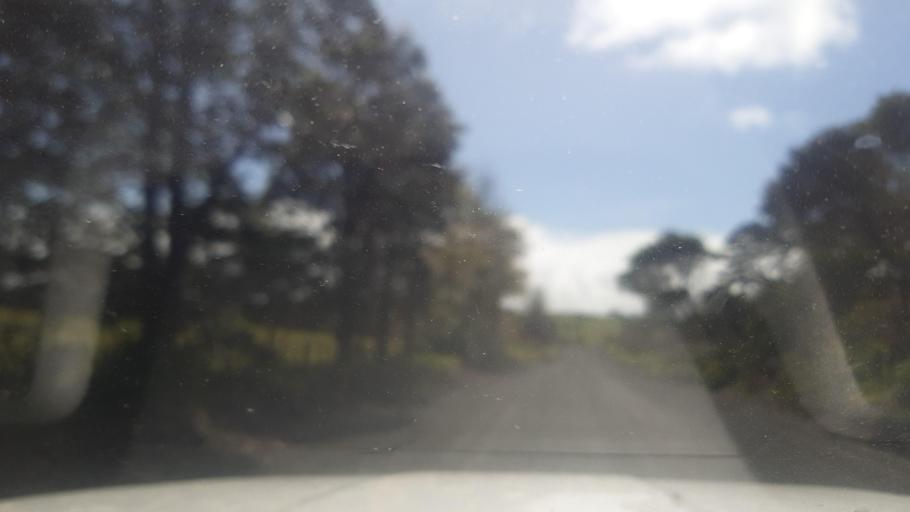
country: NZ
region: Northland
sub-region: Far North District
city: Kaitaia
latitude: -34.7486
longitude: 173.0708
